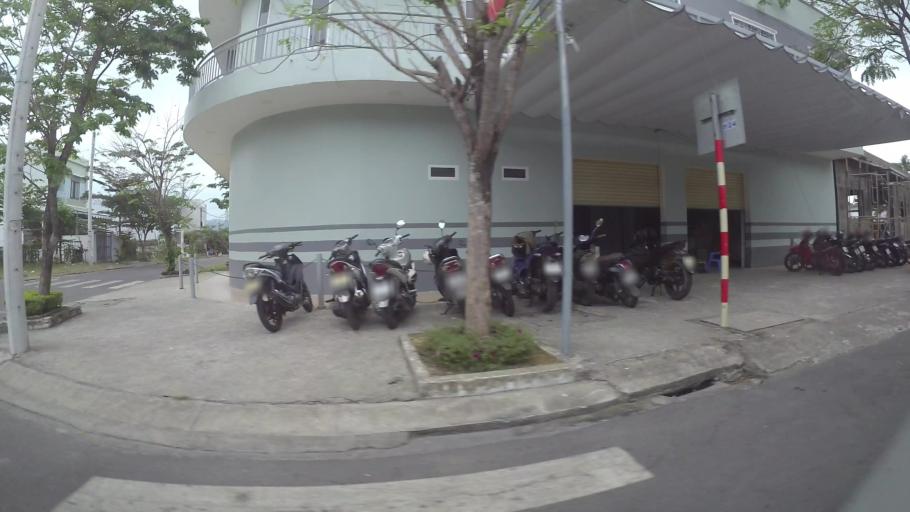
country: VN
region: Da Nang
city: Lien Chieu
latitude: 16.0519
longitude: 108.1682
